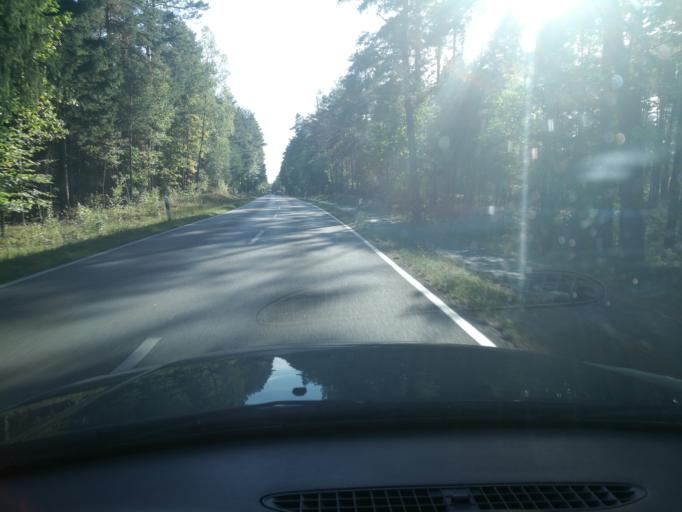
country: DE
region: Bavaria
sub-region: Regierungsbezirk Mittelfranken
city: Kalchreuth
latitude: 49.5399
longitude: 11.0889
